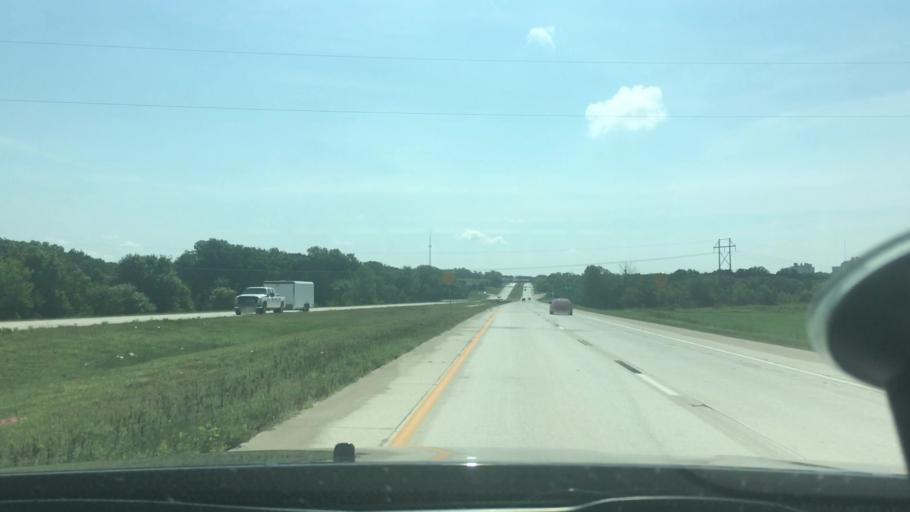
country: US
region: Oklahoma
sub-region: Pontotoc County
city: Ada
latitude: 34.7805
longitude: -96.7133
